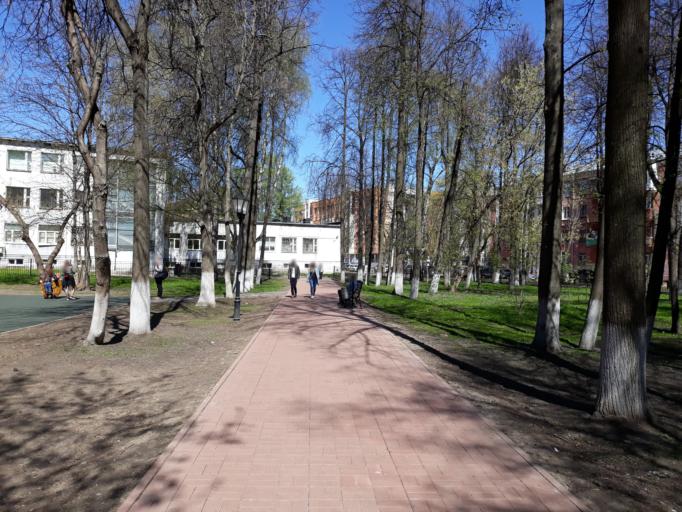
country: RU
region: Jaroslavl
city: Yaroslavl
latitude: 57.6291
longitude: 39.8730
